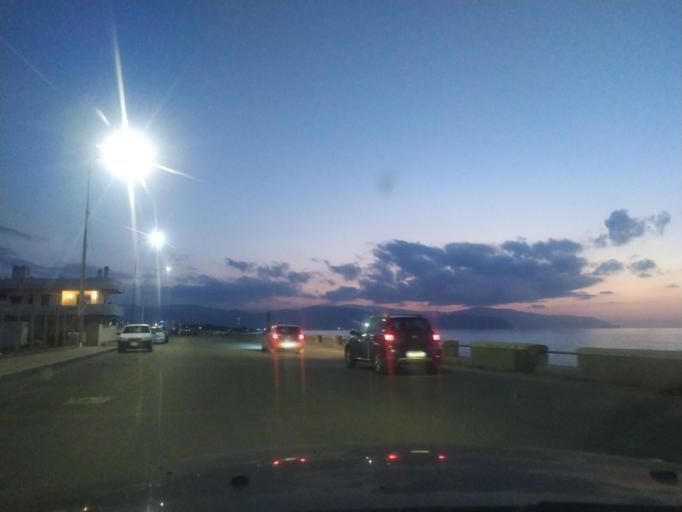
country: IT
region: Sicily
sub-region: Messina
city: Terme
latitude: 38.1464
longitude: 15.1594
